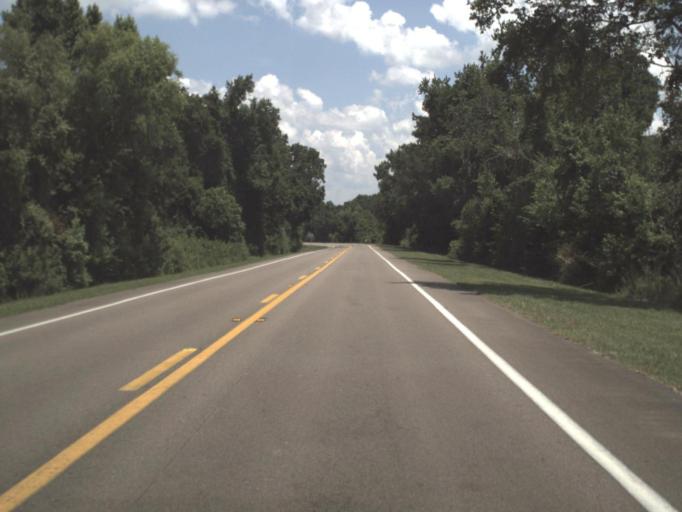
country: US
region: Florida
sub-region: Alachua County
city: Alachua
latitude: 29.8500
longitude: -82.4048
